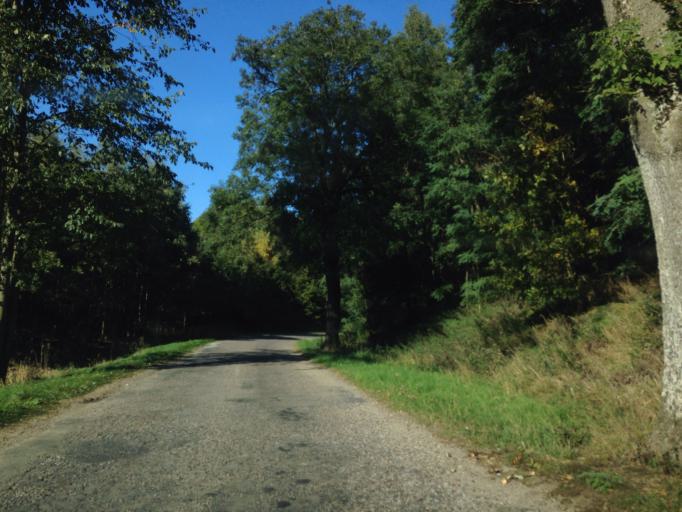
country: PL
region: Kujawsko-Pomorskie
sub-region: Powiat brodnicki
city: Gorzno
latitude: 53.2711
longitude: 19.6907
